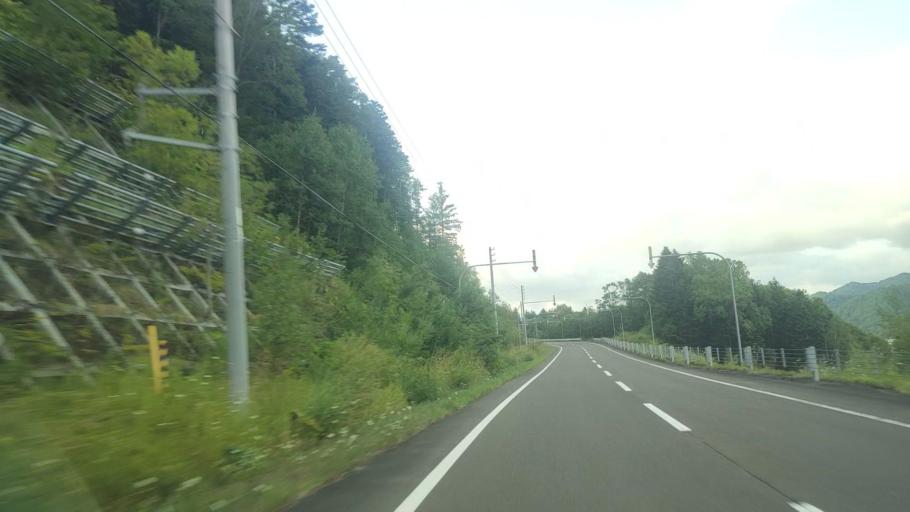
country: JP
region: Hokkaido
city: Bibai
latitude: 43.0589
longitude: 142.0987
